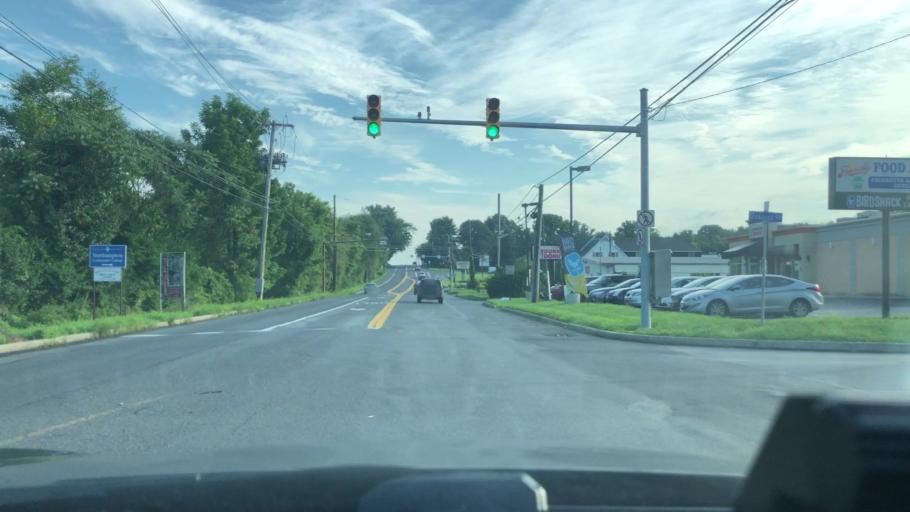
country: US
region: Pennsylvania
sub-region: Northampton County
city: Middletown
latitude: 40.6687
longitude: -75.3484
